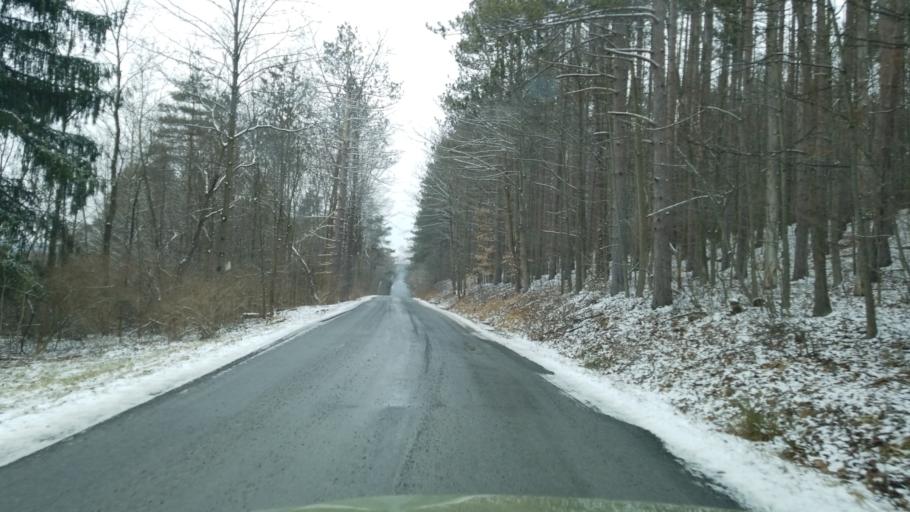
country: US
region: Pennsylvania
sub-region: Jefferson County
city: Sykesville
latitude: 41.0470
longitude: -78.7867
